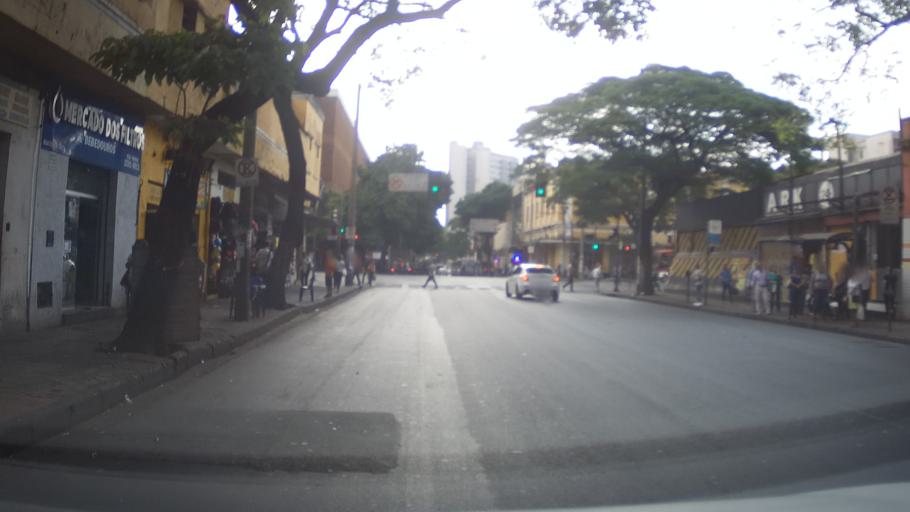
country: BR
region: Minas Gerais
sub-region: Belo Horizonte
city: Belo Horizonte
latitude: -19.9205
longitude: -43.9438
